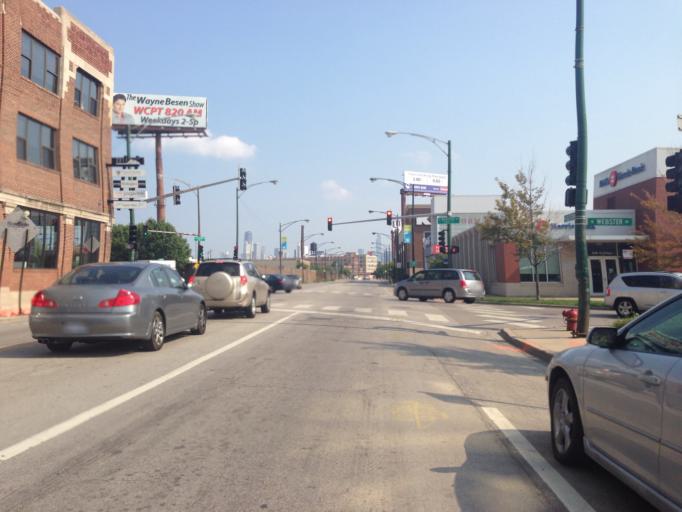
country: US
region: Illinois
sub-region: Cook County
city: Chicago
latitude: 41.9218
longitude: -87.6728
